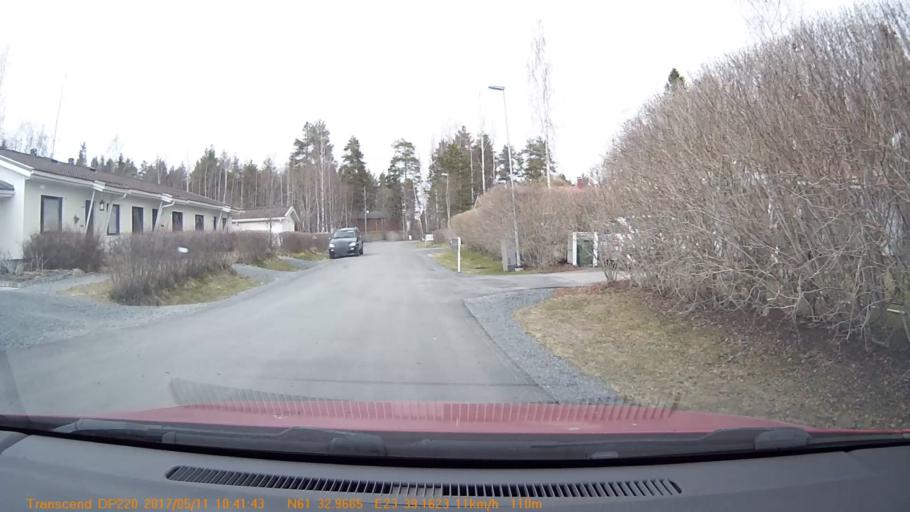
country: FI
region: Pirkanmaa
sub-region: Tampere
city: Yloejaervi
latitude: 61.5496
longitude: 23.6528
